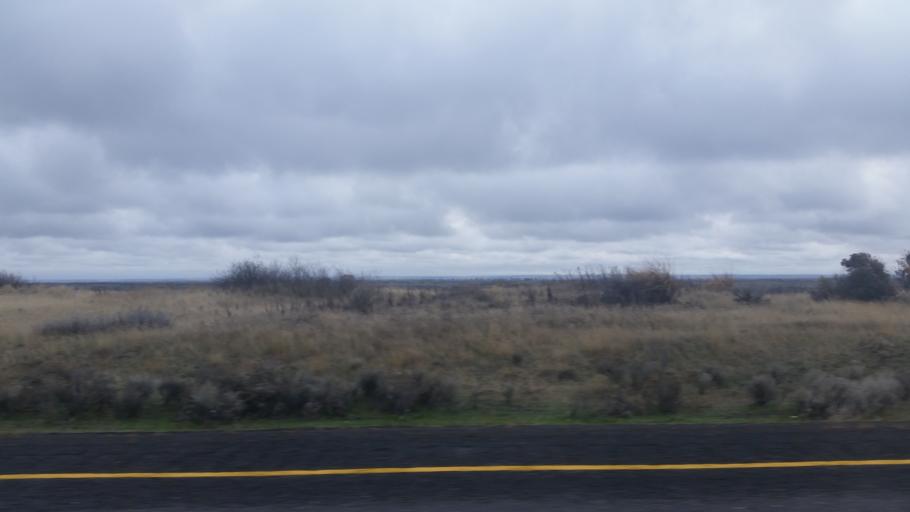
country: US
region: Washington
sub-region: Lincoln County
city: Davenport
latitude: 47.2926
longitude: -118.0337
